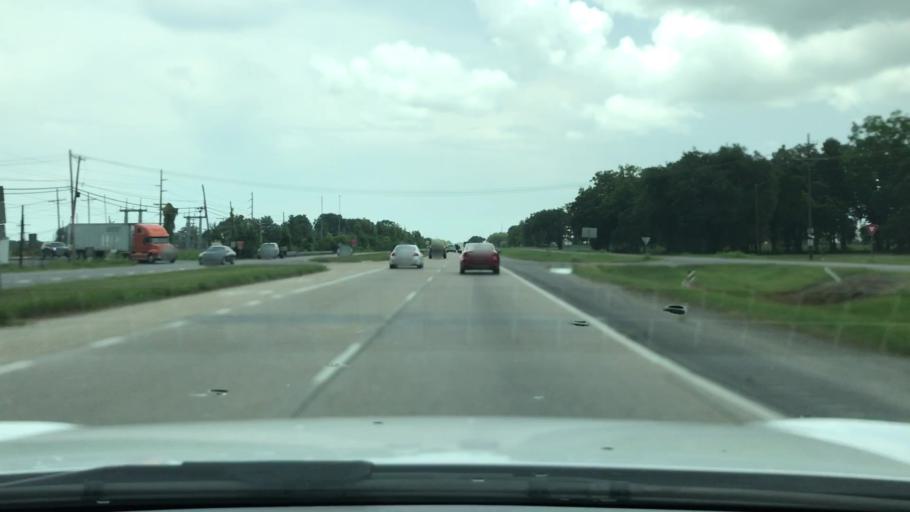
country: US
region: Louisiana
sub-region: Iberville Parish
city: Plaquemine
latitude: 30.3143
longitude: -91.2488
